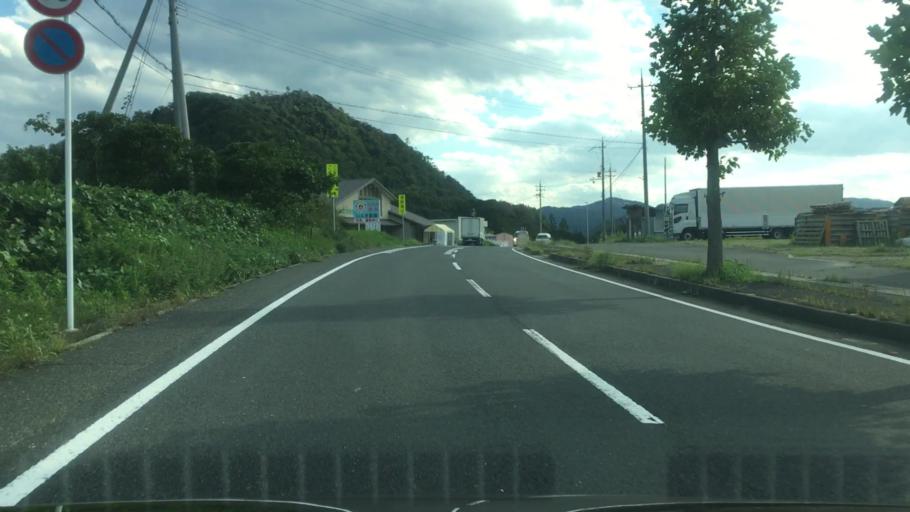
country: JP
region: Hyogo
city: Toyooka
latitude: 35.6229
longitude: 134.9284
